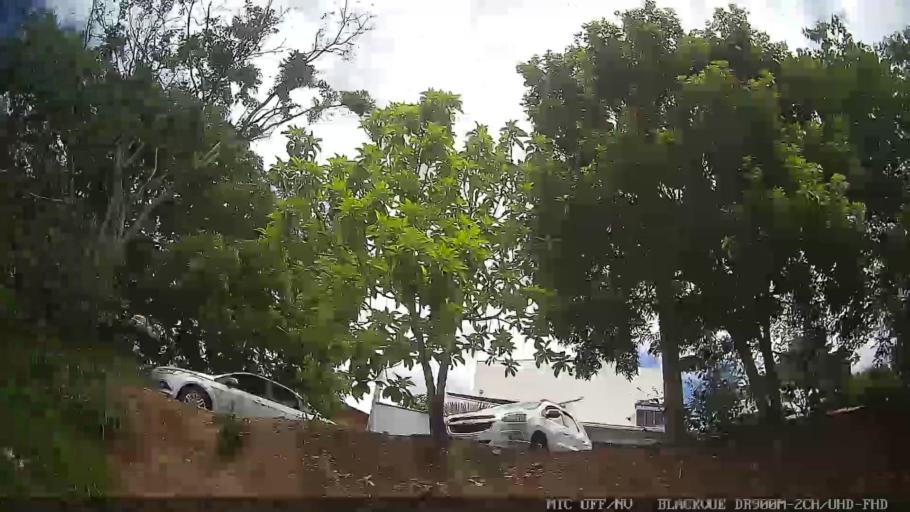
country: BR
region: Sao Paulo
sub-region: Jaguariuna
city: Jaguariuna
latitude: -22.7006
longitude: -46.9620
